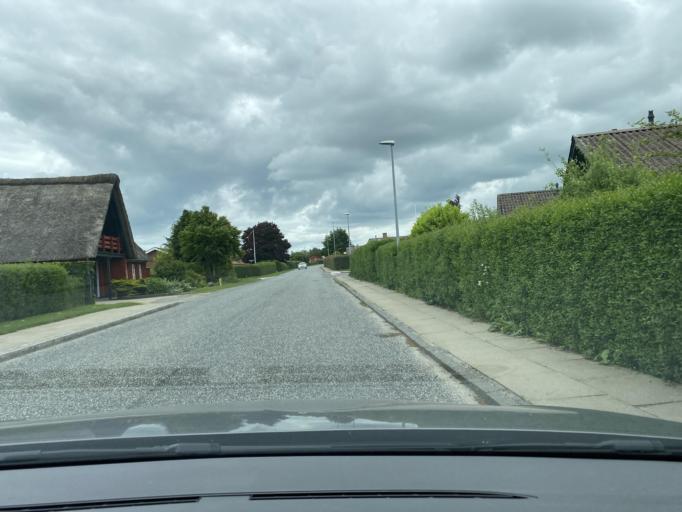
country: DK
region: South Denmark
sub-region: Vejle Kommune
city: Vejle
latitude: 55.6583
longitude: 9.4958
